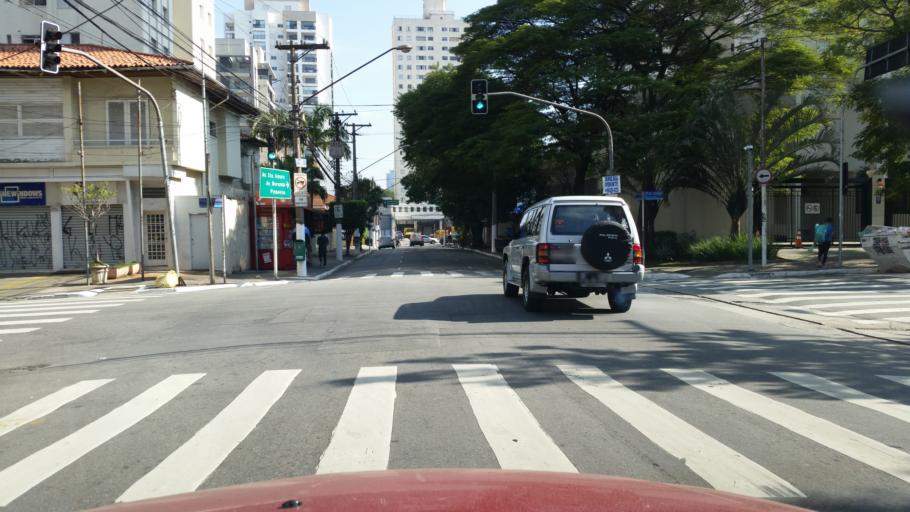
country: BR
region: Sao Paulo
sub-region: Diadema
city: Diadema
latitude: -23.6226
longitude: -46.6831
